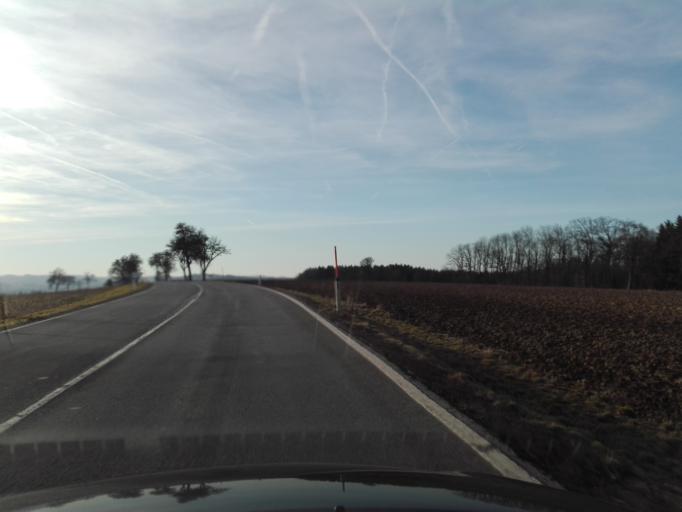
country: AT
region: Lower Austria
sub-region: Politischer Bezirk Amstetten
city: Strengberg
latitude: 48.1401
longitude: 14.6972
